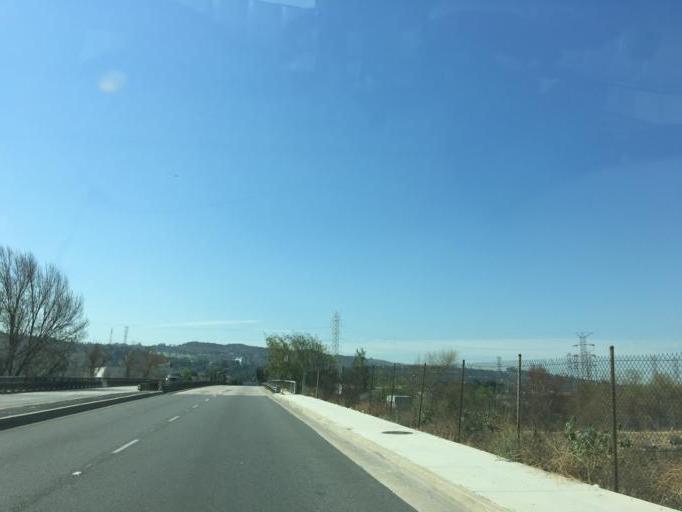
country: US
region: California
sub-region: Los Angeles County
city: South El Monte
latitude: 34.0350
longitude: -118.0384
